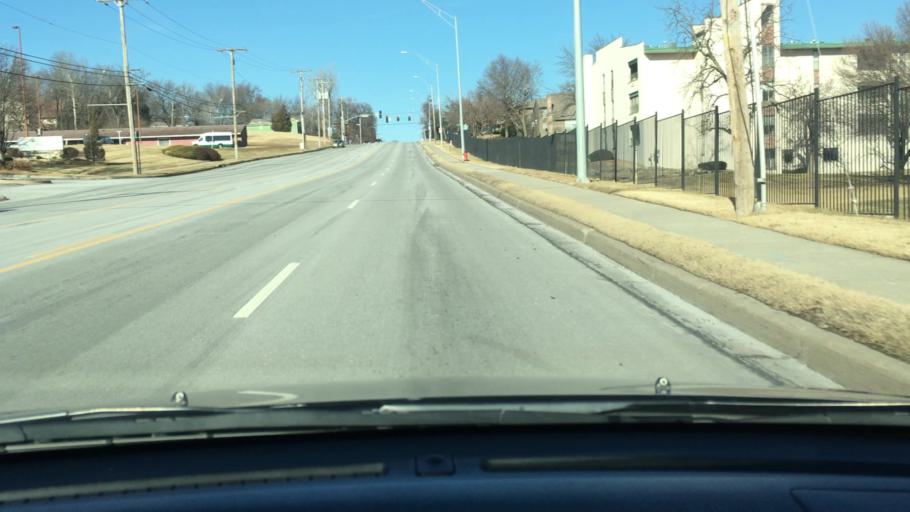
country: US
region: Kansas
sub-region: Johnson County
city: Leawood
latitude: 38.9467
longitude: -94.5963
